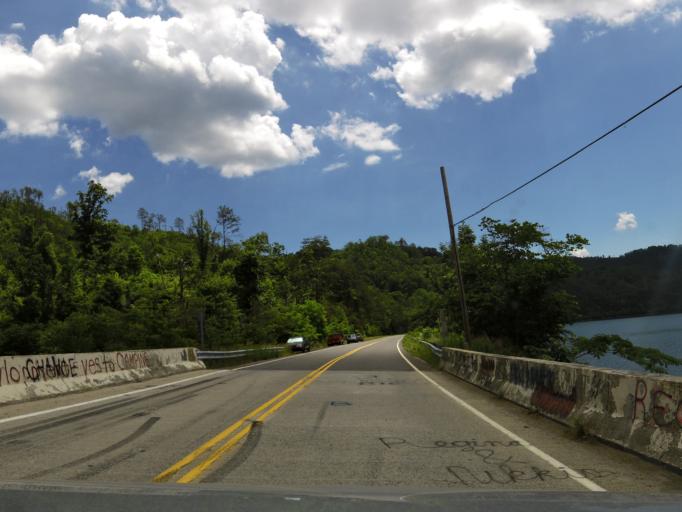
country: US
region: Tennessee
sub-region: Blount County
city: Maryville
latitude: 35.5555
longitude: -83.9986
